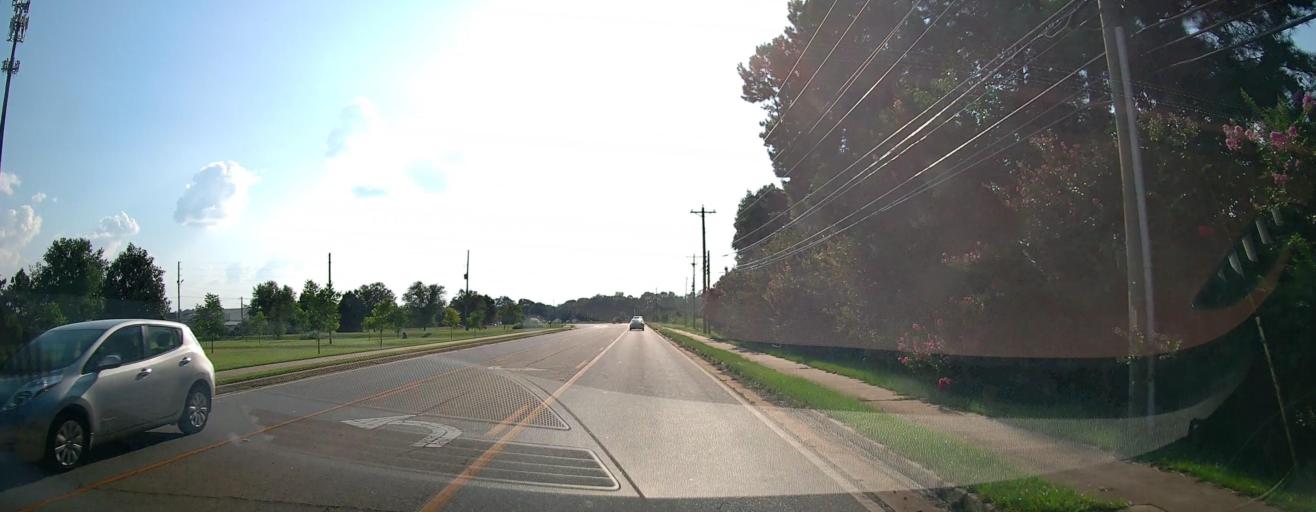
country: US
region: Georgia
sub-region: Houston County
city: Perry
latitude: 32.5062
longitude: -83.6572
